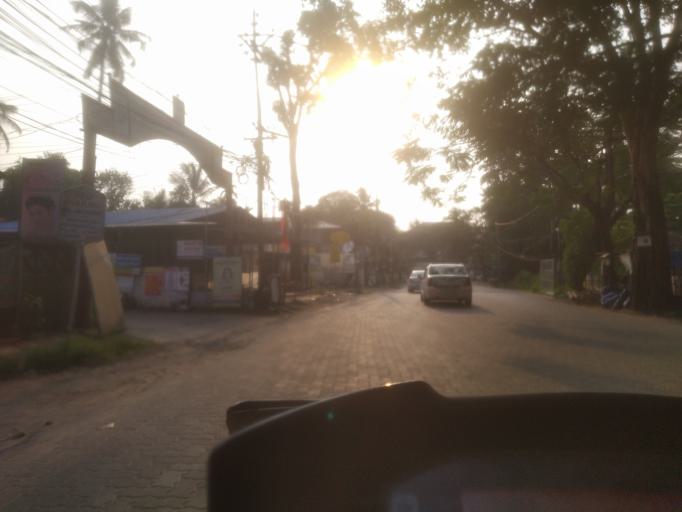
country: IN
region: Kerala
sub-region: Ernakulam
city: Cochin
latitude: 9.9424
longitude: 76.3347
